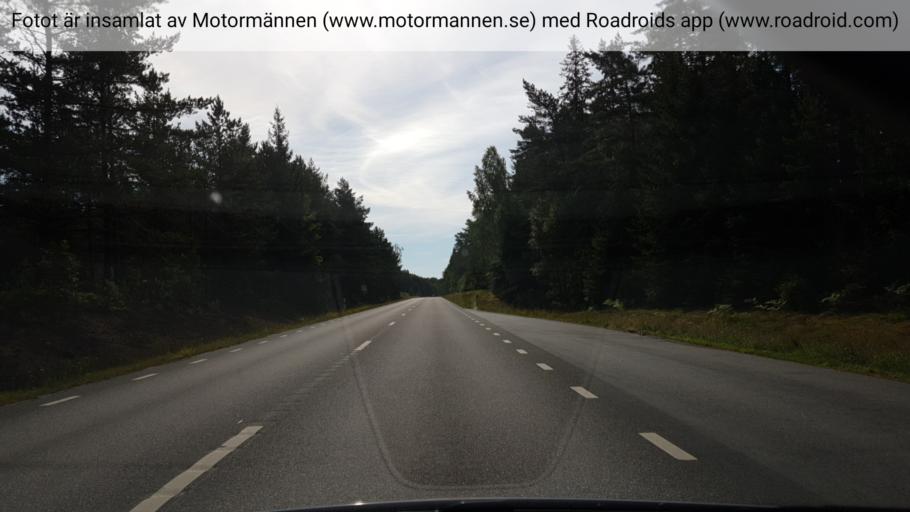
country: SE
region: Vaestra Goetaland
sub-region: Hjo Kommun
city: Hjo
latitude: 58.3375
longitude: 14.2377
